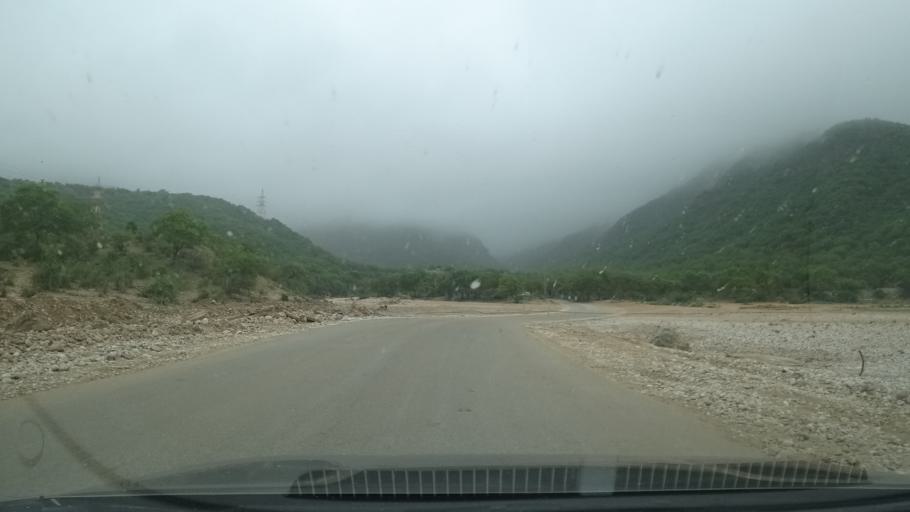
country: OM
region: Zufar
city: Salalah
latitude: 17.1026
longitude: 54.0761
